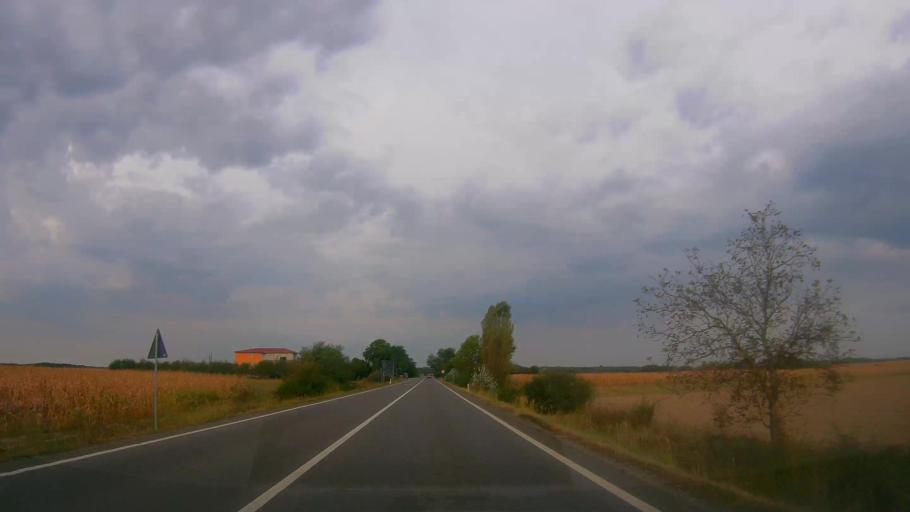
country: RO
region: Satu Mare
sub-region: Comuna Turulung
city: Draguseni
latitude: 47.8763
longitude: 23.0668
